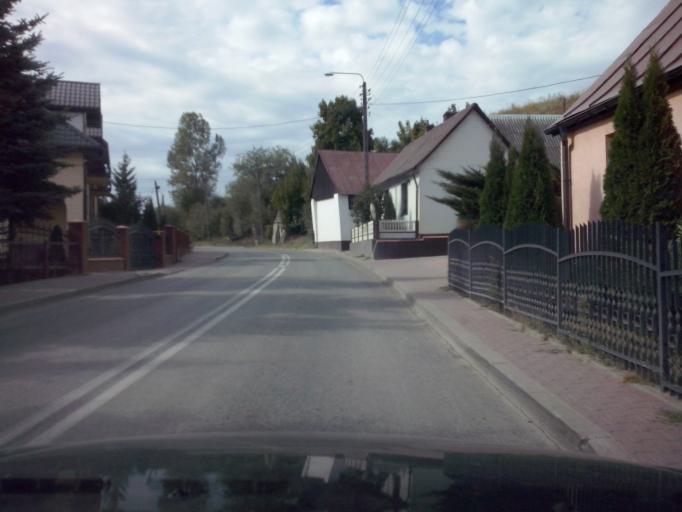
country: PL
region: Swietokrzyskie
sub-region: Powiat kielecki
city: Lagow
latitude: 50.7809
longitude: 21.0849
